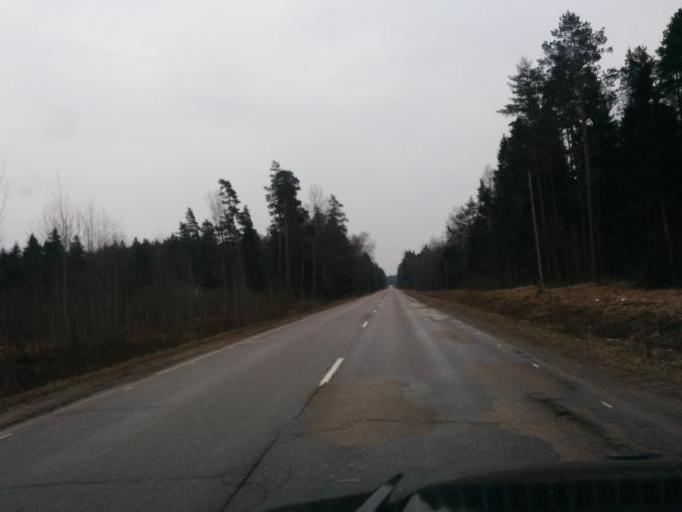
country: LV
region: Ikskile
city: Ikskile
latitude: 56.8121
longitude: 24.4802
